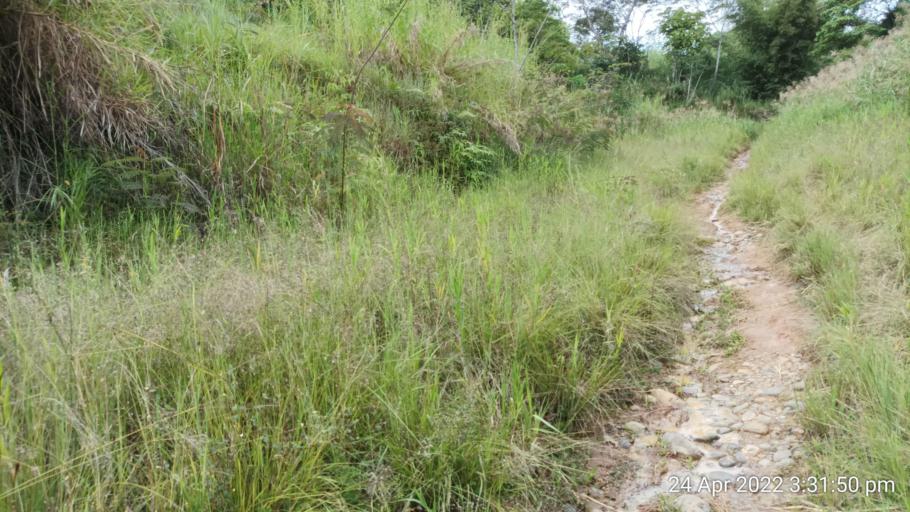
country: PG
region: Jiwaka
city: Minj
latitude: -5.8906
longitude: 144.8199
